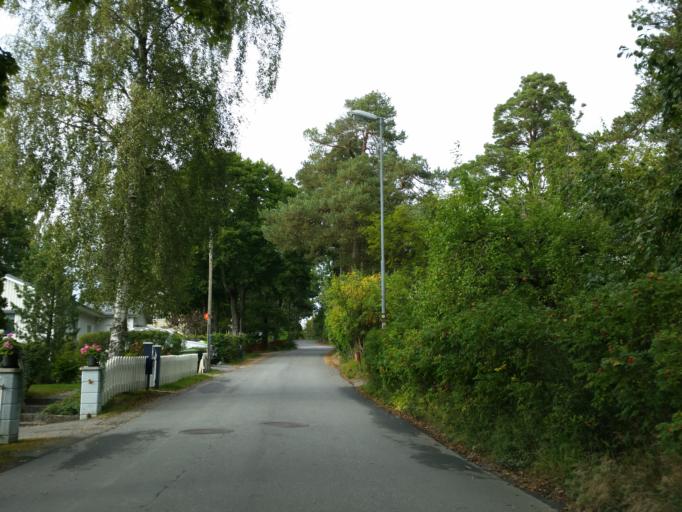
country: SE
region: Stockholm
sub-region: Sollentuna Kommun
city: Sollentuna
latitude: 59.4556
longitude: 17.9301
